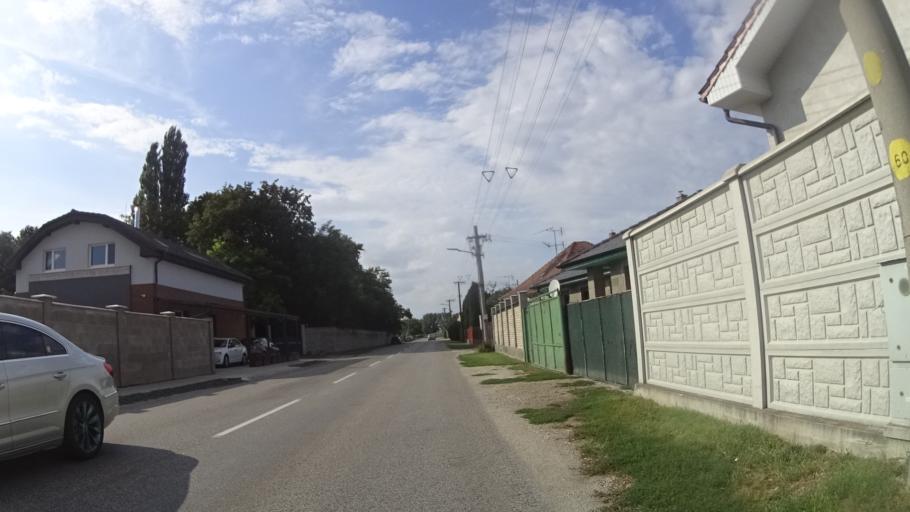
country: SK
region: Trnavsky
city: Gabcikovo
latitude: 47.9221
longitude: 17.4972
